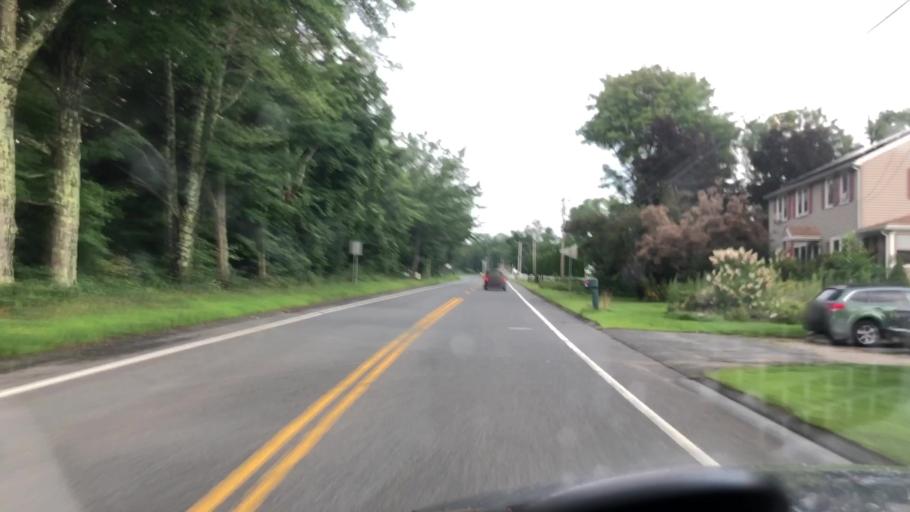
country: US
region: Massachusetts
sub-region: Hampshire County
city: Westhampton
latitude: 42.2884
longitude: -72.7451
